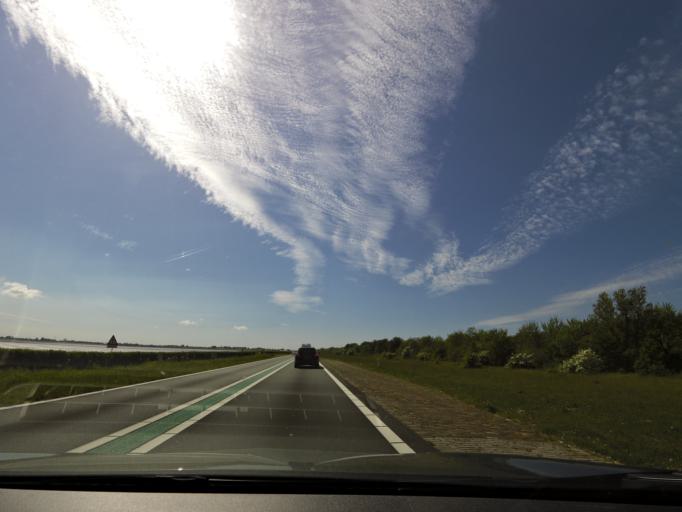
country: NL
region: Zeeland
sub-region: Schouwen-Duiveland
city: Bruinisse
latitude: 51.6761
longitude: 4.1279
